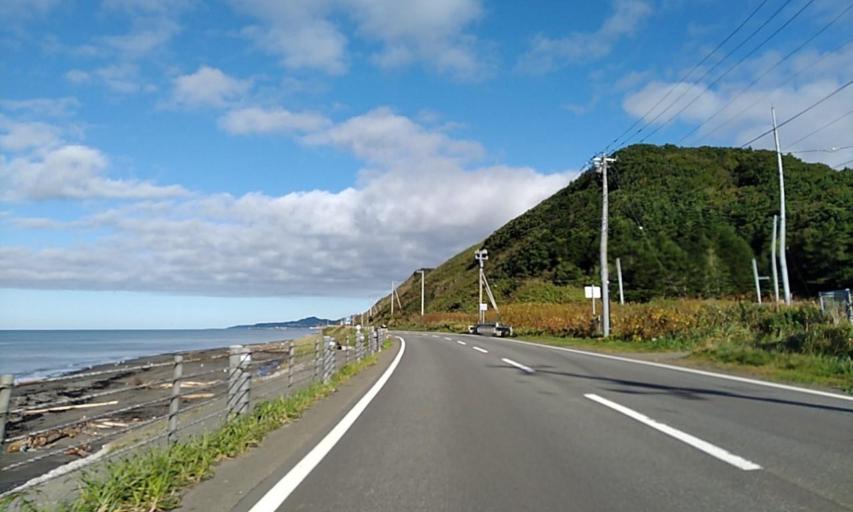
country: JP
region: Hokkaido
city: Shizunai-furukawacho
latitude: 42.2063
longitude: 142.6539
